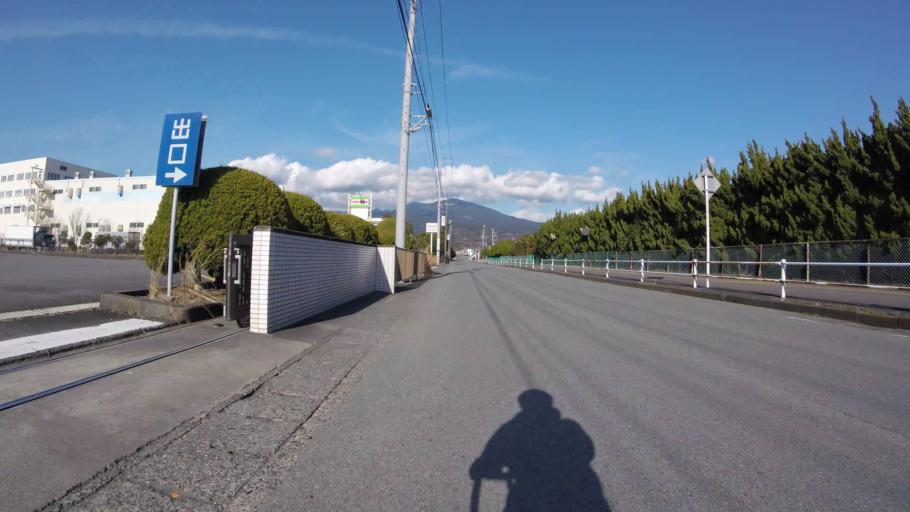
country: JP
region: Shizuoka
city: Numazu
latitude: 35.1315
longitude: 138.7809
